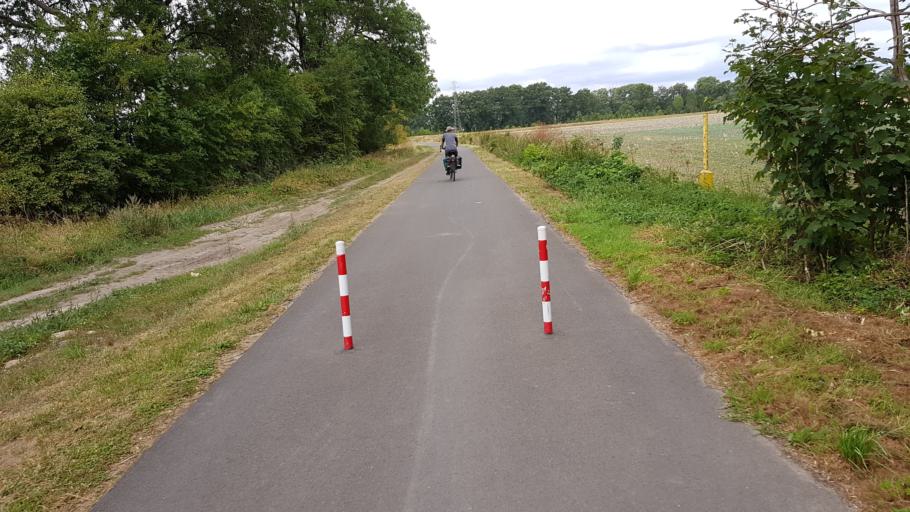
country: PL
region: West Pomeranian Voivodeship
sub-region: Powiat pyrzycki
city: Pyrzyce
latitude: 53.1424
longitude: 14.9611
